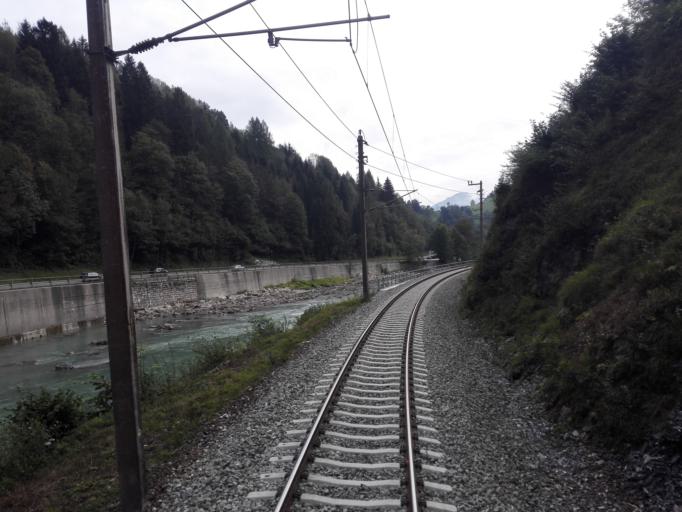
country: AT
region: Salzburg
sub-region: Politischer Bezirk Sankt Johann im Pongau
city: Goldegg
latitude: 47.3096
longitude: 13.1177
